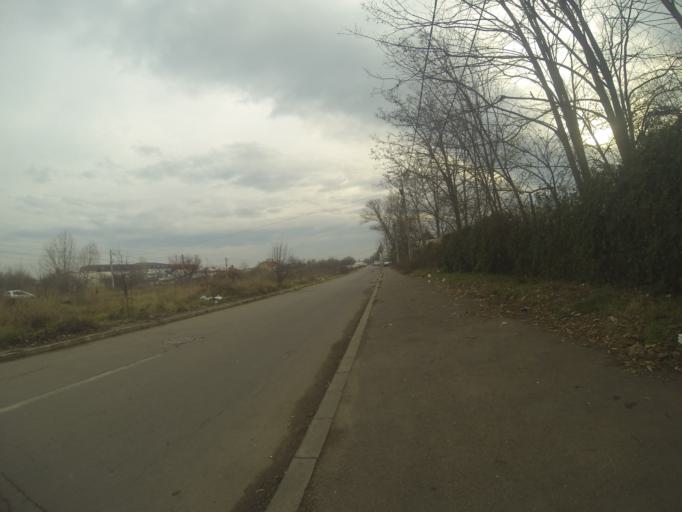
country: RO
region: Ilfov
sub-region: Comuna Jilava
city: Jilava
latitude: 44.3759
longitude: 26.0866
